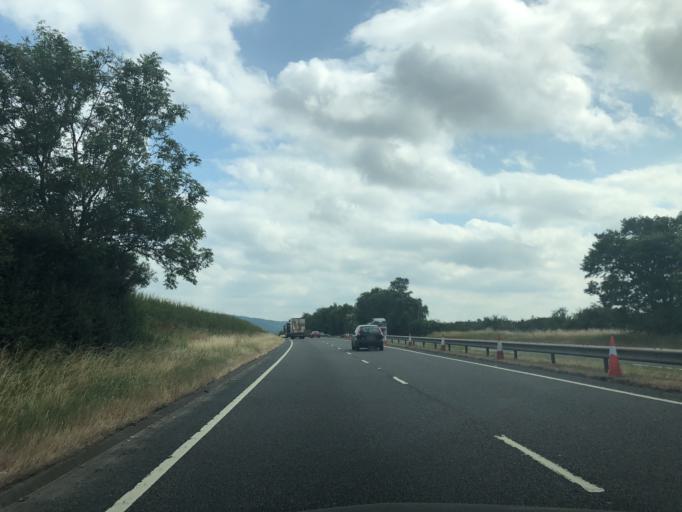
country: GB
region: England
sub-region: Stockton-on-Tees
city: Yarm
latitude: 54.4349
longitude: -1.3236
